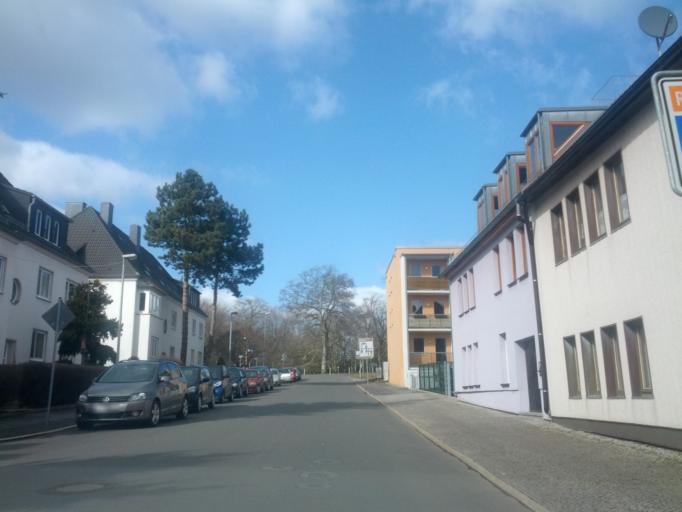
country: DE
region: Thuringia
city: Gotha
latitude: 50.9431
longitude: 10.7089
